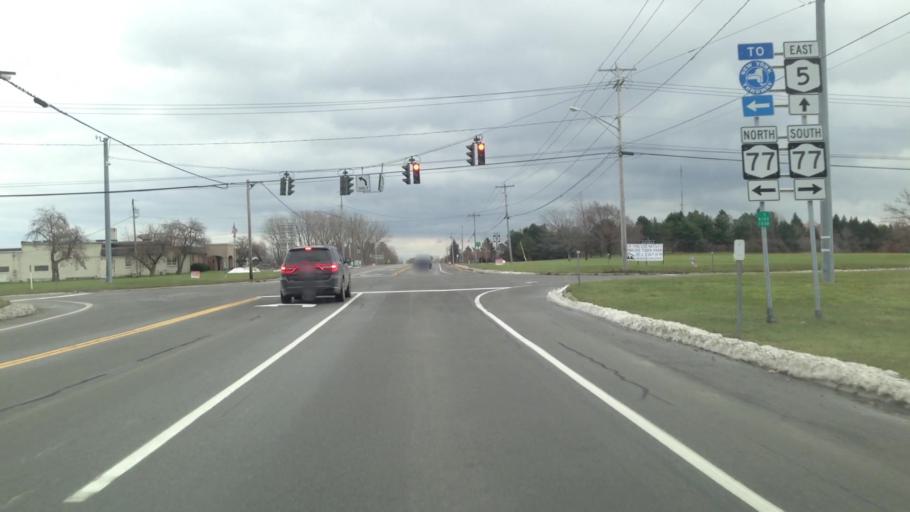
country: US
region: New York
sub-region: Erie County
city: Akron
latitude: 42.9930
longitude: -78.4066
